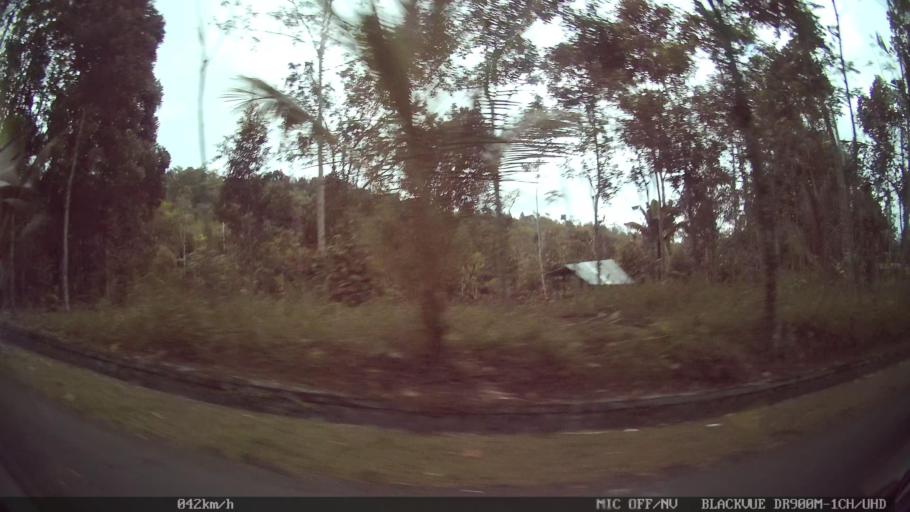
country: ID
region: Bali
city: Banjar Bias
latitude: -8.3727
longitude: 115.4315
